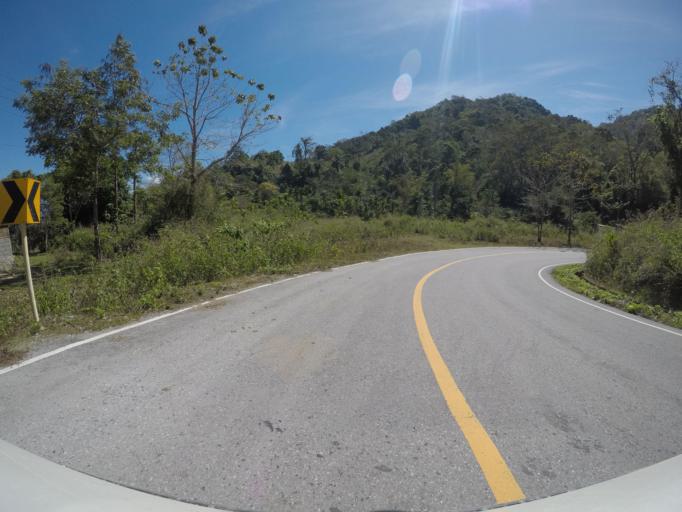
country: TL
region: Manufahi
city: Same
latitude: -8.9072
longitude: 125.9758
